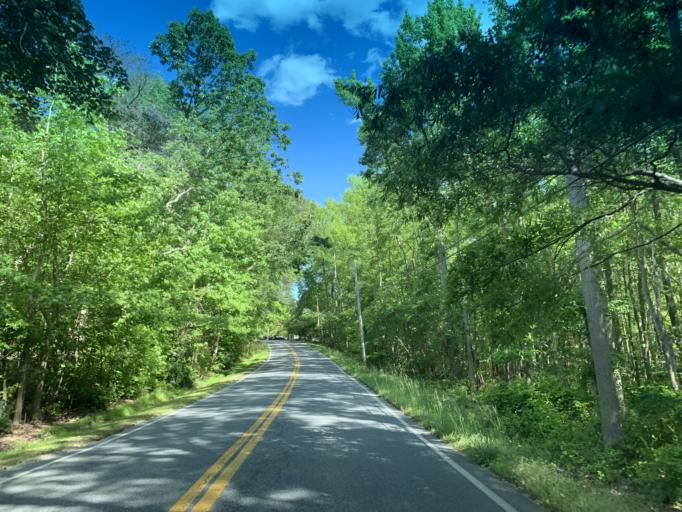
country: US
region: Maryland
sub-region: Cecil County
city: Charlestown
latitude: 39.5426
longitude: -75.9281
